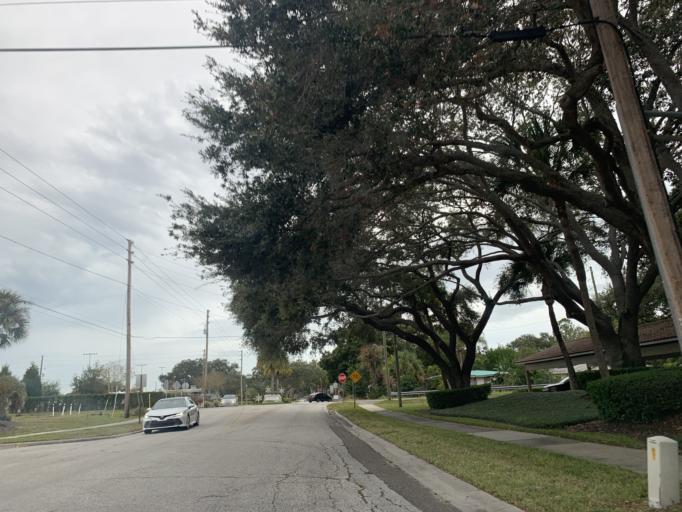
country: US
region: Florida
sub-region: Pinellas County
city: Belleair
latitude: 27.9352
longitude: -82.7998
